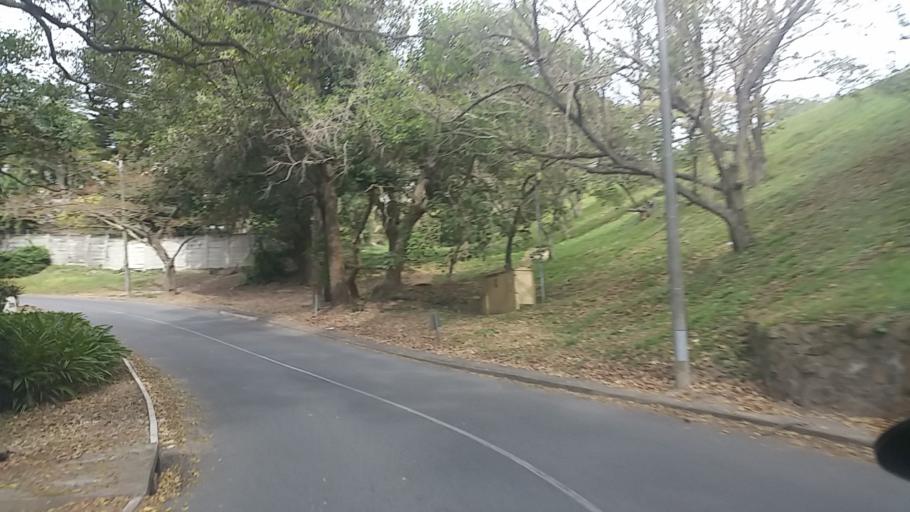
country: ZA
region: KwaZulu-Natal
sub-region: eThekwini Metropolitan Municipality
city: Berea
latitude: -29.8432
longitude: 30.9280
